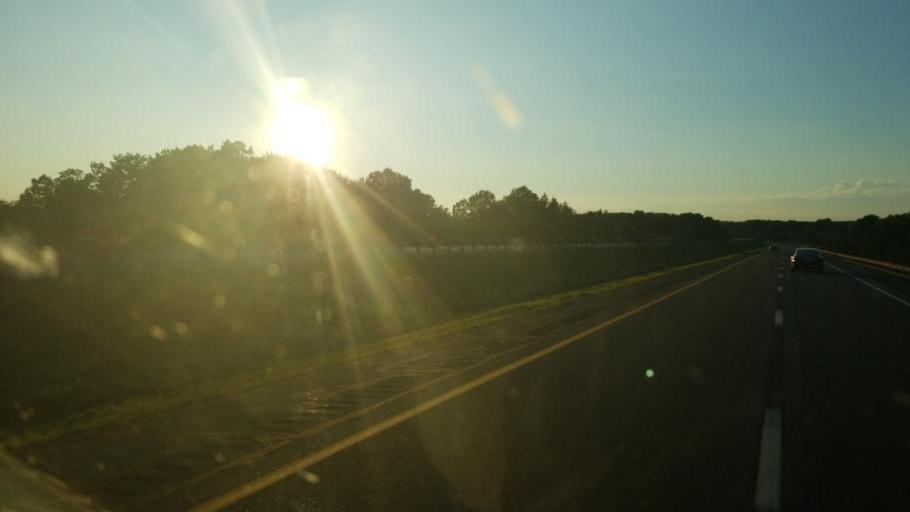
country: US
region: Ohio
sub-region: Mahoning County
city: Austintown
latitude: 41.0714
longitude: -80.7926
